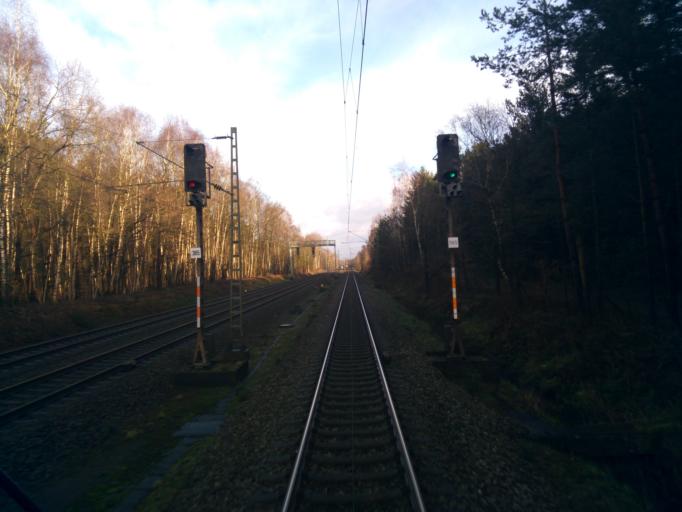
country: DE
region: Lower Saxony
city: Hemsbunde
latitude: 53.1361
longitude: 9.4512
